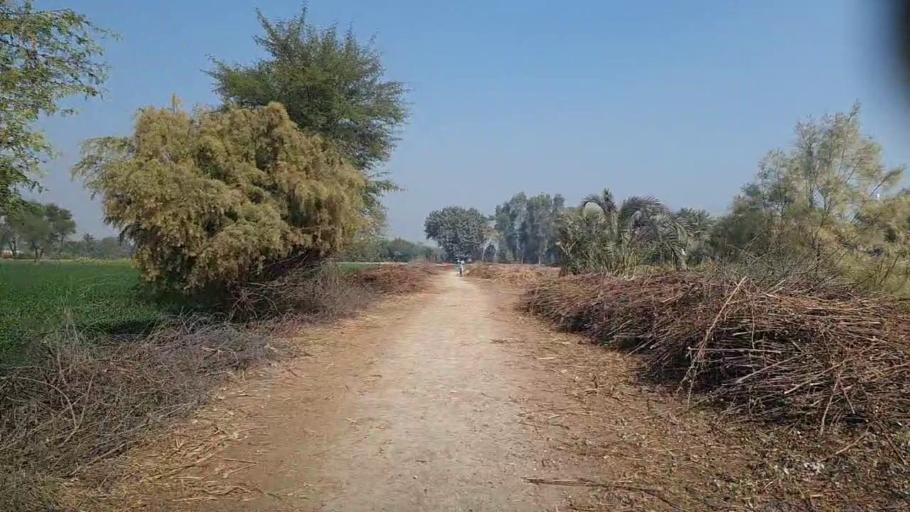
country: PK
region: Sindh
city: Khairpur
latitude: 27.9336
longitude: 69.6707
